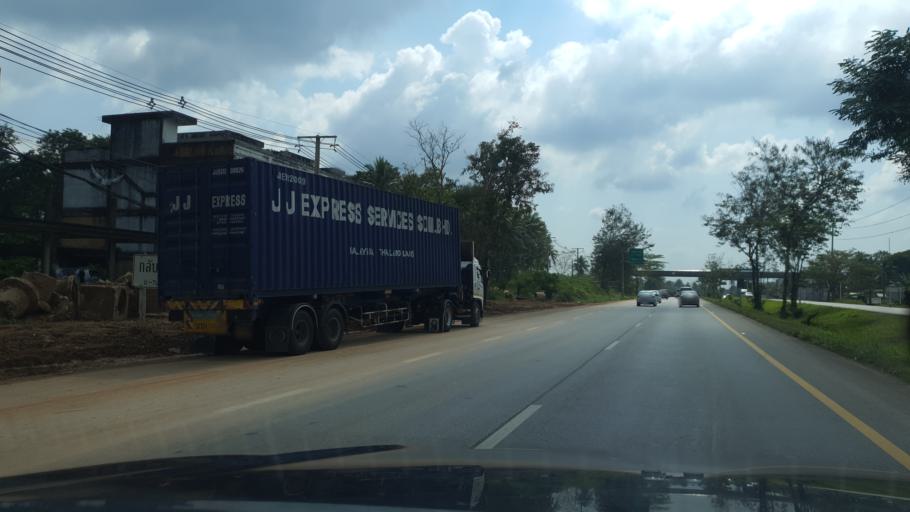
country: TH
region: Chumphon
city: Chumphon
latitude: 10.4572
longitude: 99.1327
